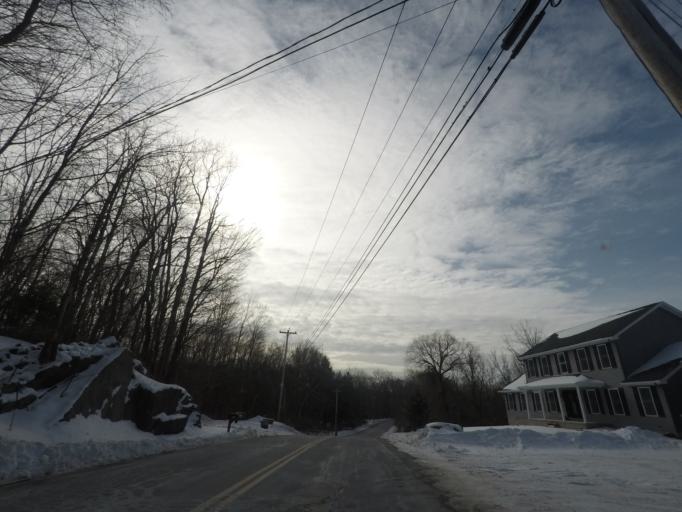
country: US
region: New York
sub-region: Rensselaer County
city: Averill Park
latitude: 42.5667
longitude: -73.4928
